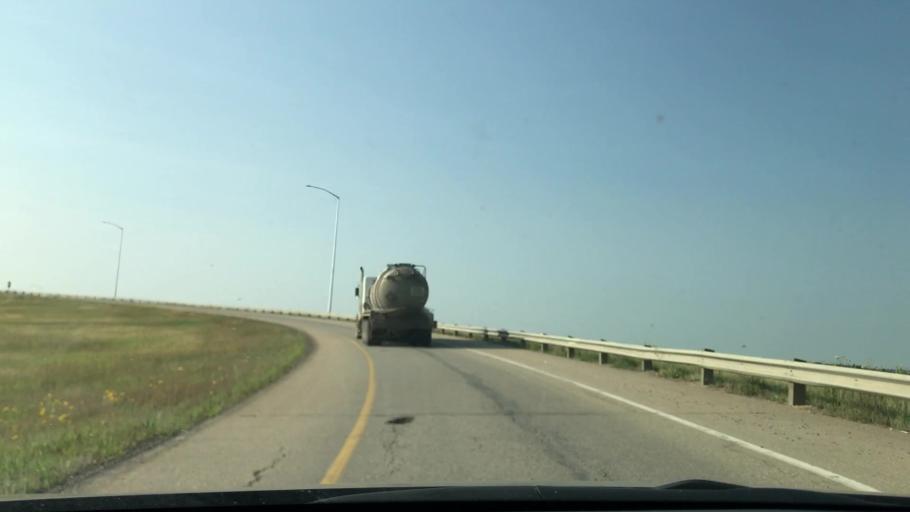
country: CA
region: Alberta
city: Leduc
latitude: 53.2866
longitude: -113.5518
